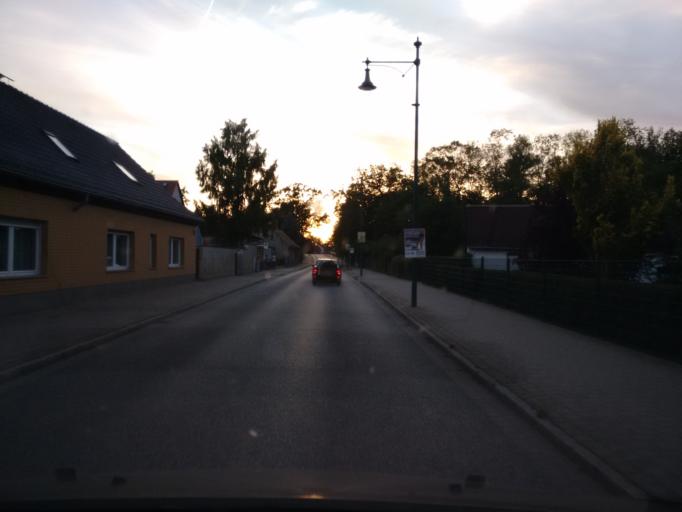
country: DE
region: Brandenburg
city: Beeskow
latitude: 52.1680
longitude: 14.2572
